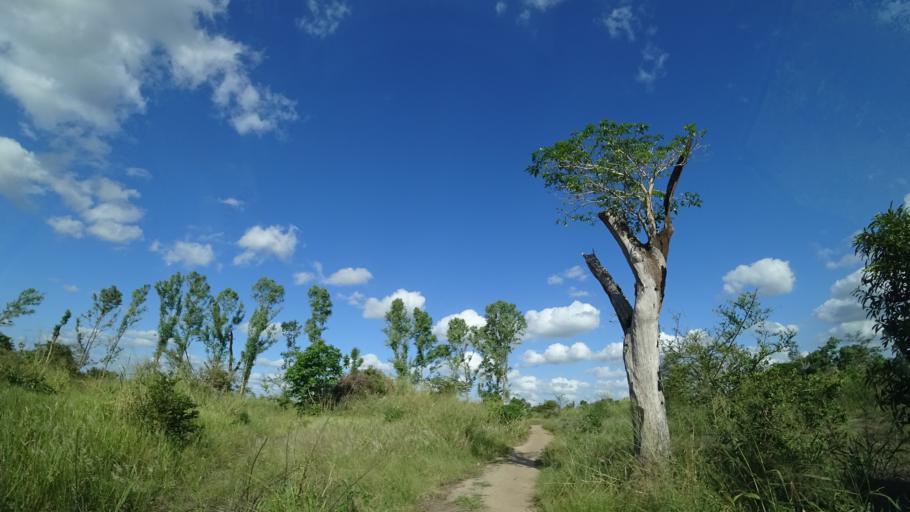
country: MZ
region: Sofala
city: Dondo
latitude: -19.4290
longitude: 34.7264
